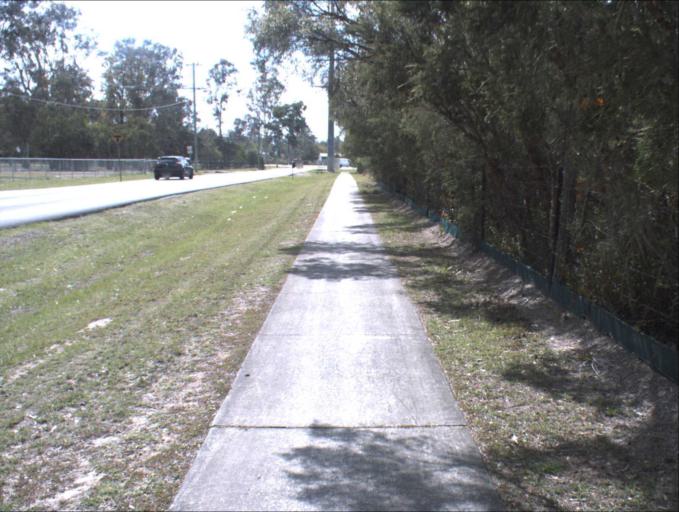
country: AU
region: Queensland
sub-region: Logan
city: Logan City
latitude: -27.6658
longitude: 153.0905
